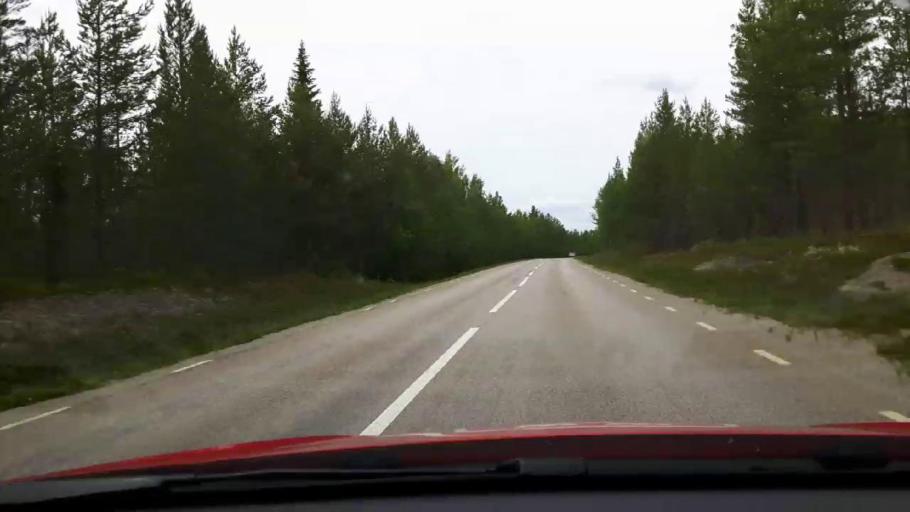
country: SE
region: Jaemtland
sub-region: Harjedalens Kommun
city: Sveg
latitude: 62.2430
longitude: 13.8460
